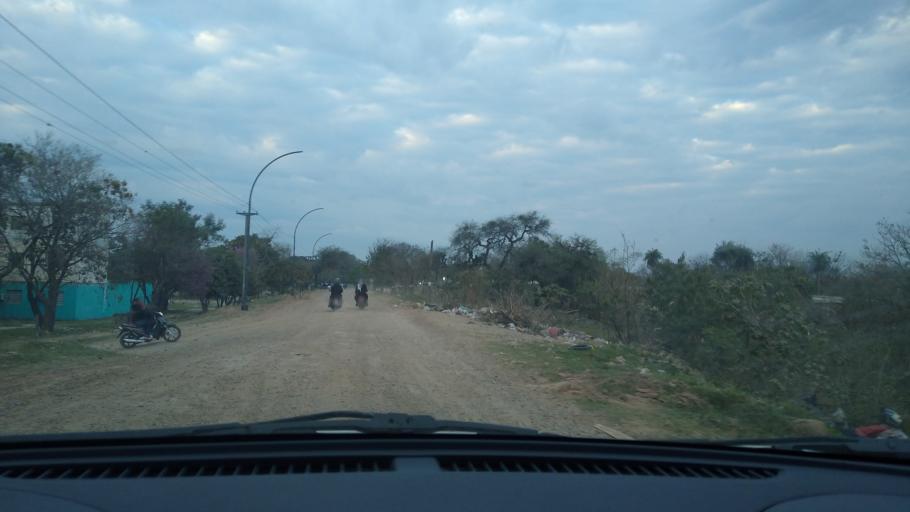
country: AR
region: Chaco
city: Barranqueras
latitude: -27.4615
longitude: -58.9511
